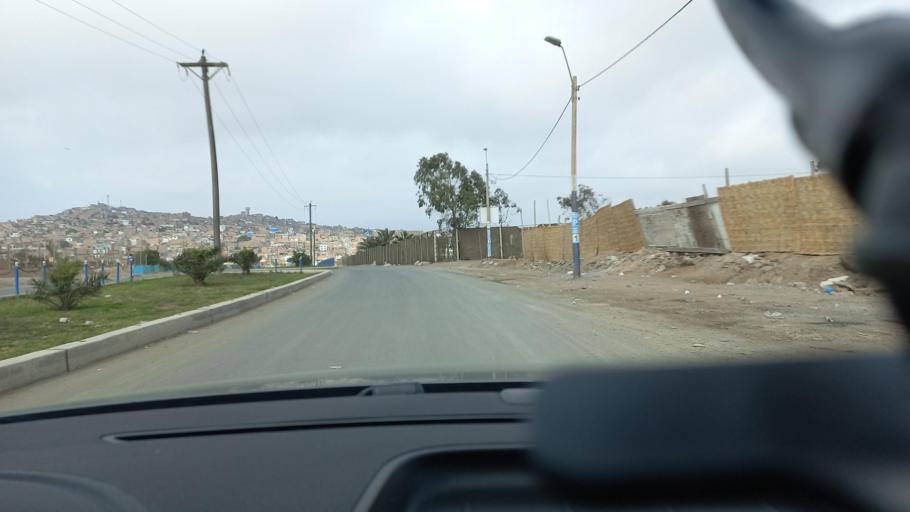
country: PE
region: Lima
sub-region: Lima
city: Surco
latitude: -12.2040
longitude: -76.9995
